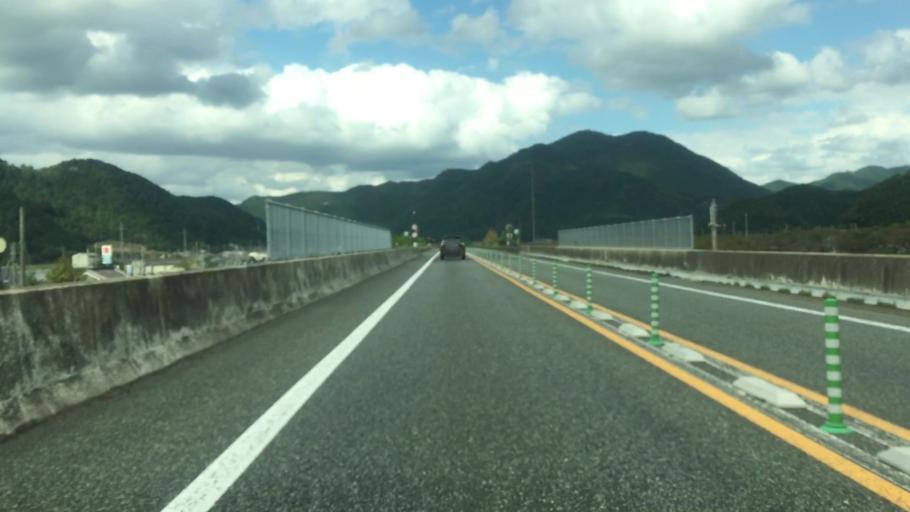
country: JP
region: Kyoto
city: Fukuchiyama
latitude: 35.2152
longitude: 135.0356
